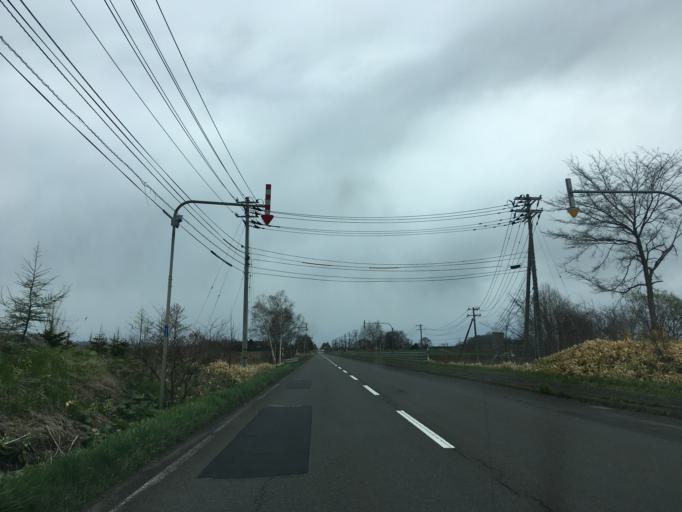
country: JP
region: Hokkaido
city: Chitose
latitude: 42.9074
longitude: 141.8120
